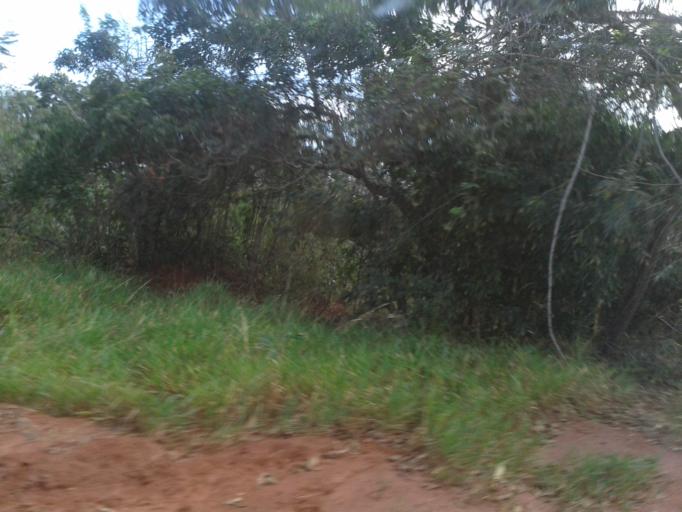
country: BR
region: Minas Gerais
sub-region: Ituiutaba
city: Ituiutaba
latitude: -19.0578
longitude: -49.3636
